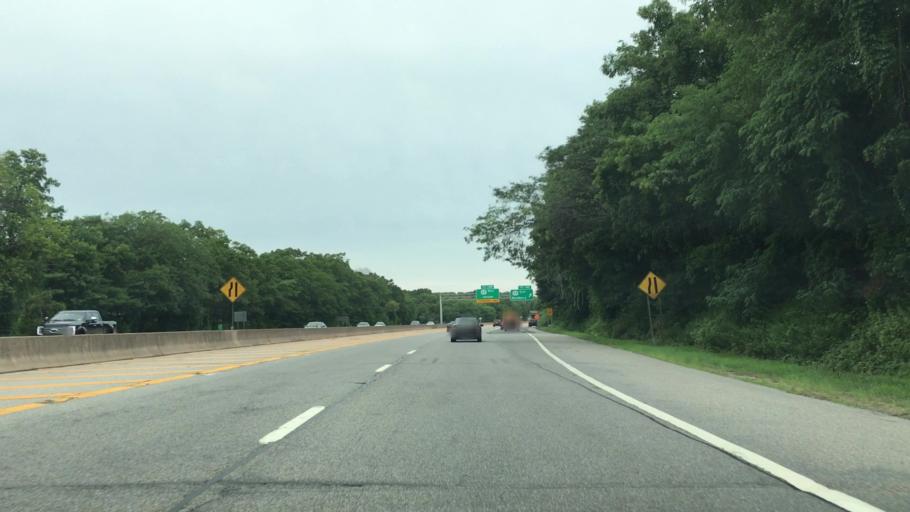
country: US
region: New York
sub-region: Nassau County
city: Syosset
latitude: 40.8069
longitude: -73.4911
